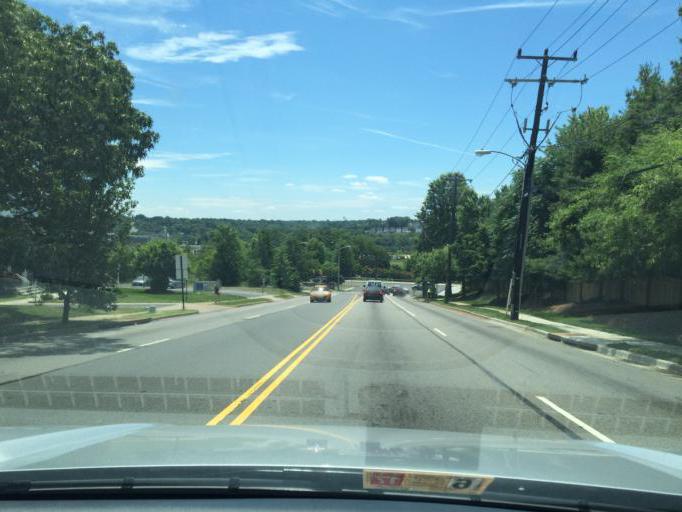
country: US
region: Virginia
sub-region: Fairfax County
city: Huntington
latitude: 38.8097
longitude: -77.0887
